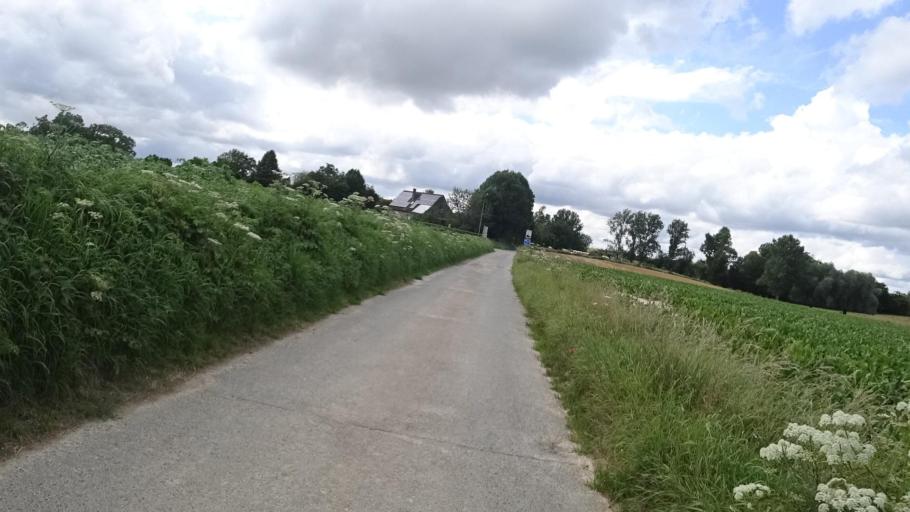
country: BE
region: Wallonia
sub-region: Province du Brabant Wallon
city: Chastre
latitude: 50.5936
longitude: 4.6477
